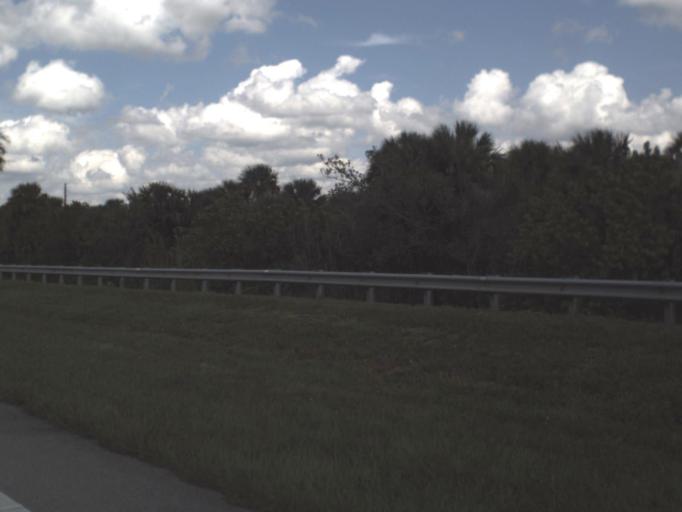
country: US
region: Florida
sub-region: Collier County
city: Immokalee
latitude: 26.2913
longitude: -81.3425
